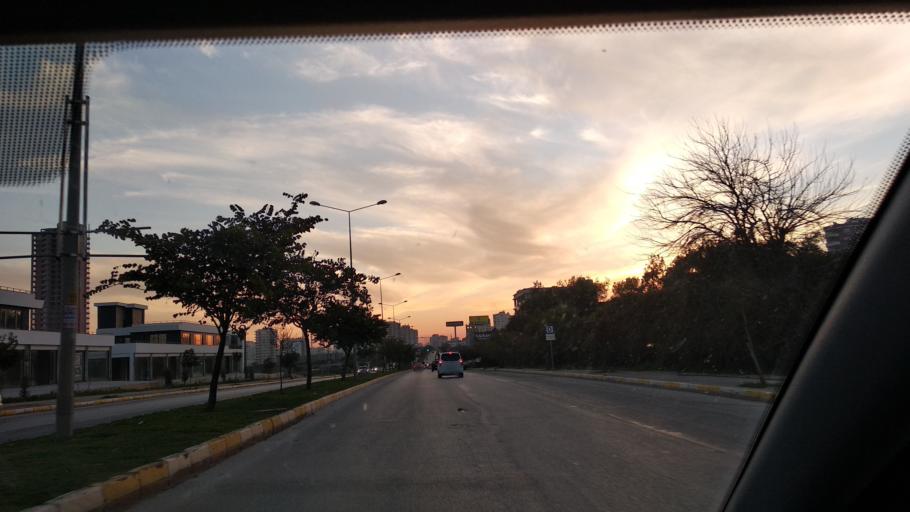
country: TR
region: Mersin
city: Mercin
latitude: 36.7990
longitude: 34.5801
